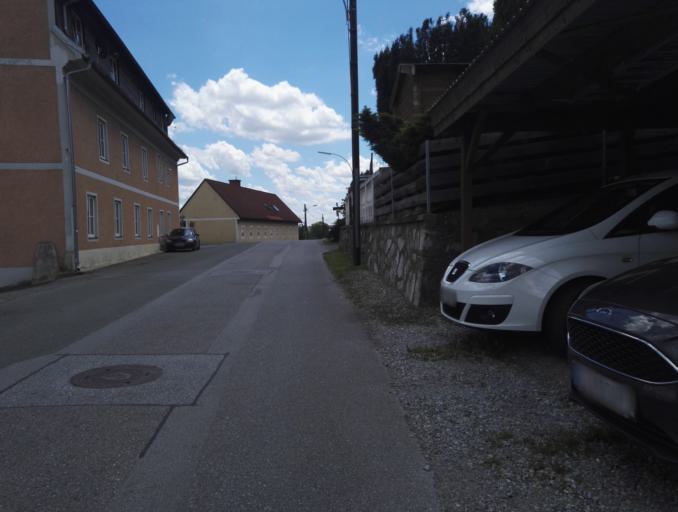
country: AT
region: Styria
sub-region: Graz Stadt
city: Goesting
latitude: 47.0870
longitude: 15.4024
